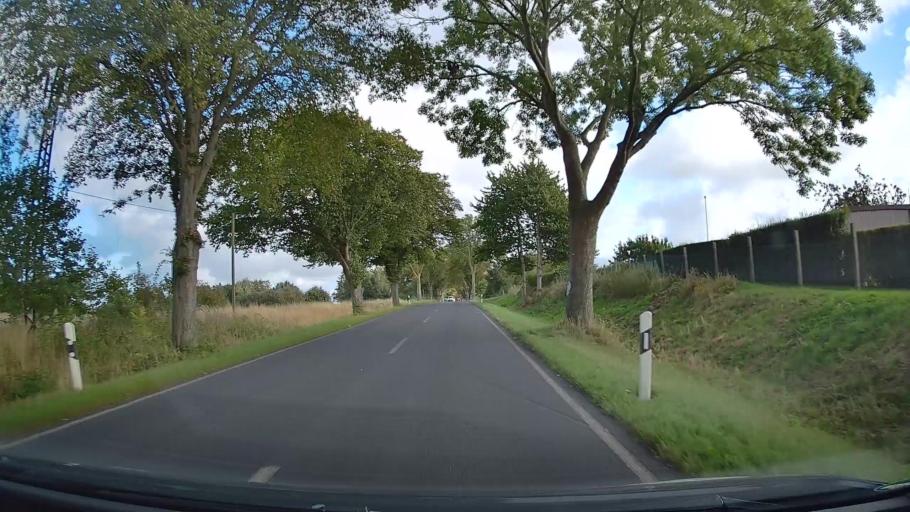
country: DE
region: Mecklenburg-Vorpommern
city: Bergen auf Ruegen
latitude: 54.4083
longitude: 13.4436
